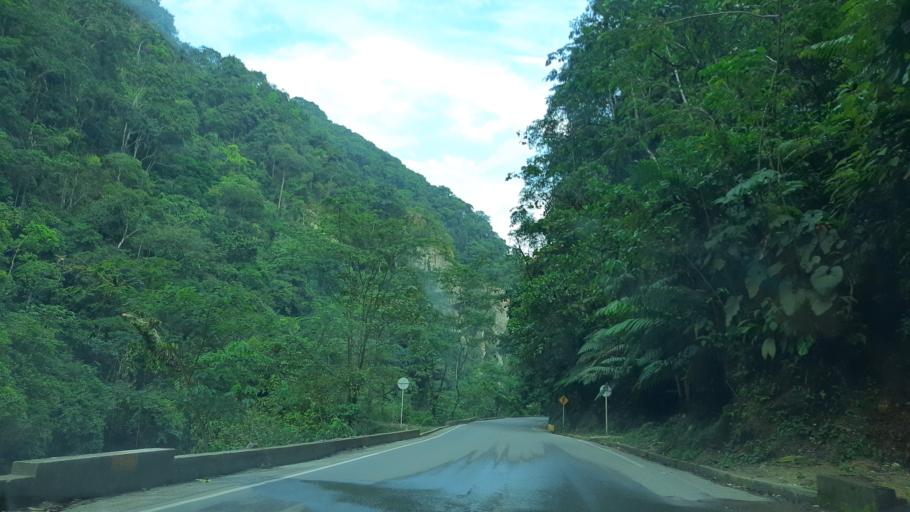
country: CO
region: Boyaca
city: Santa Maria
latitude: 4.8510
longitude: -73.2291
